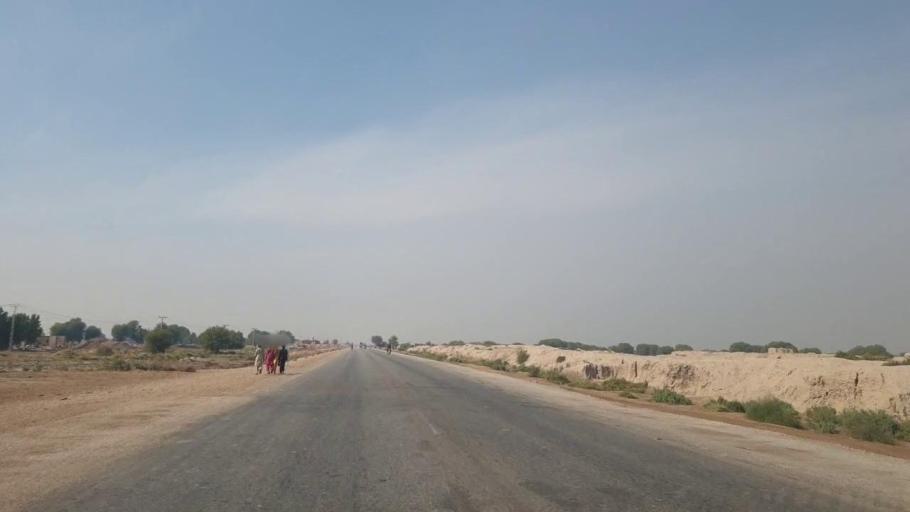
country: PK
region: Sindh
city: Sann
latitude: 25.9872
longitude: 68.1800
